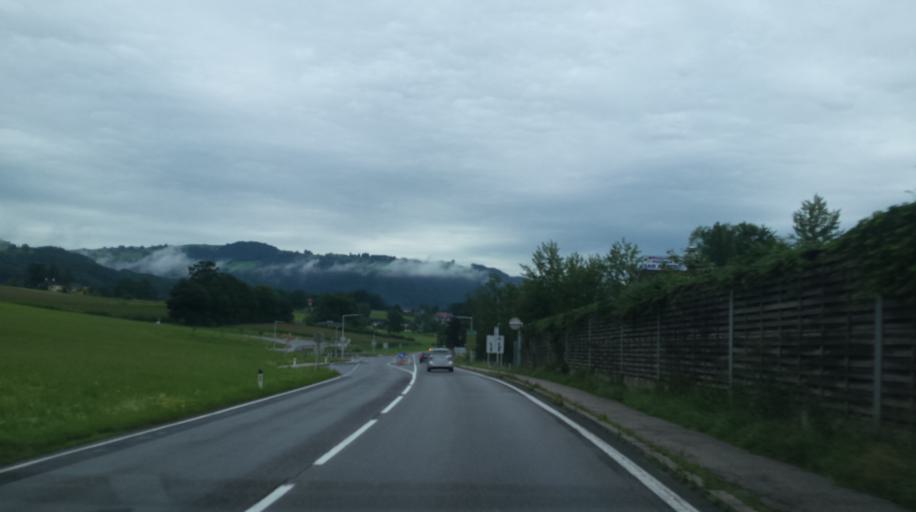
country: AT
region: Upper Austria
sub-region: Politischer Bezirk Gmunden
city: Altmunster
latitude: 47.8791
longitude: 13.7751
